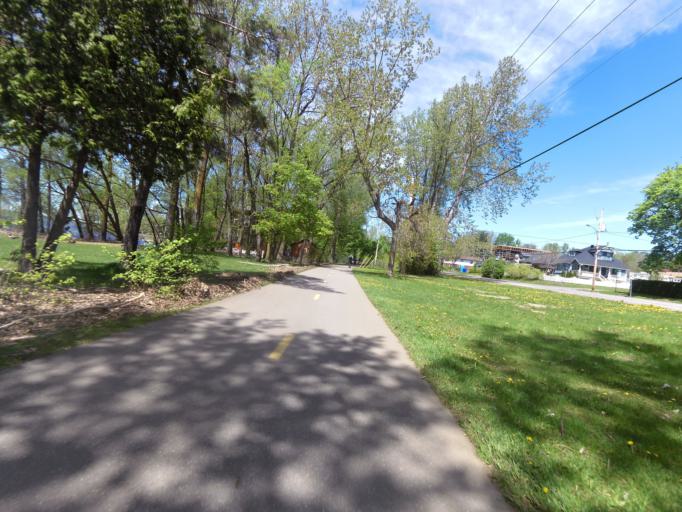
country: CA
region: Ontario
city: Bells Corners
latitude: 45.4005
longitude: -75.8642
